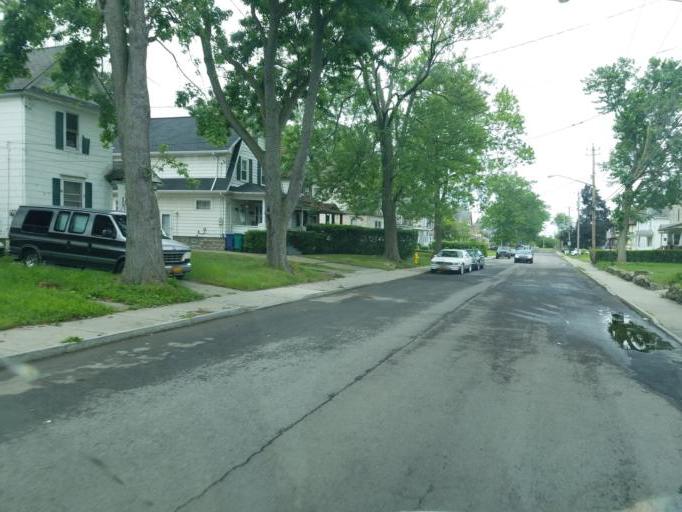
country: CA
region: Ontario
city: Niagara Falls
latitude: 43.1174
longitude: -79.0527
